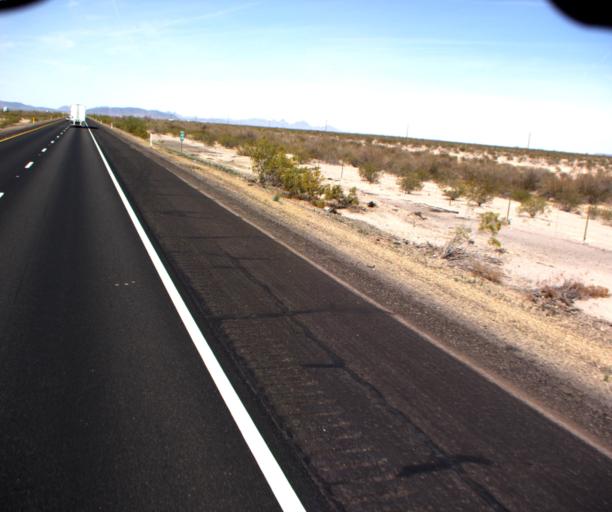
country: US
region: Arizona
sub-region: La Paz County
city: Salome
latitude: 33.6220
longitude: -113.7044
